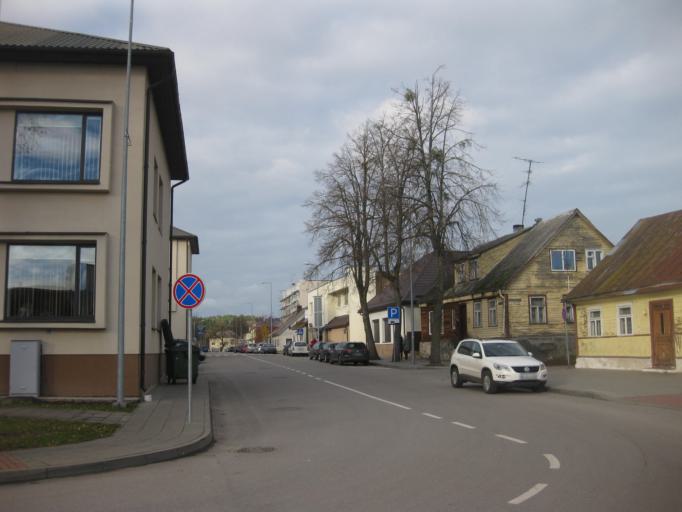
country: LT
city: Prienai
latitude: 54.6356
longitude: 23.9475
